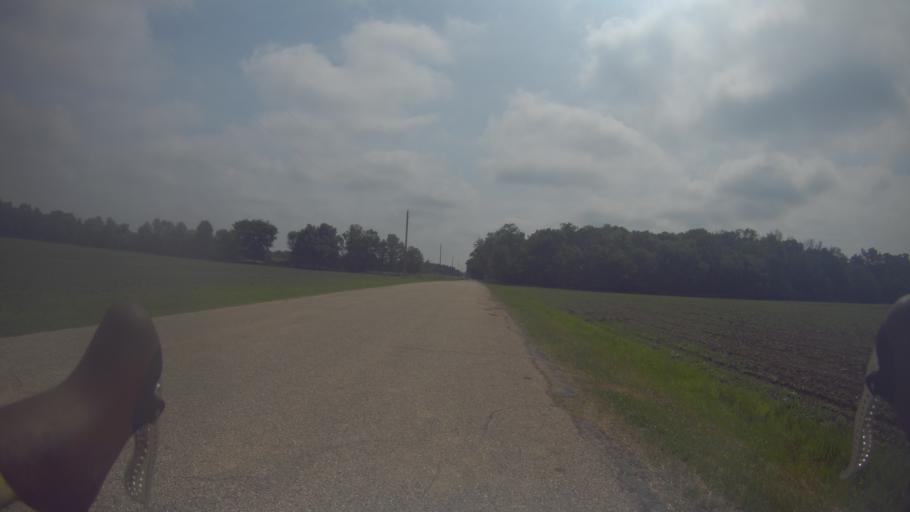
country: US
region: Wisconsin
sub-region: Jefferson County
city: Cambridge
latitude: 42.9233
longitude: -89.0198
